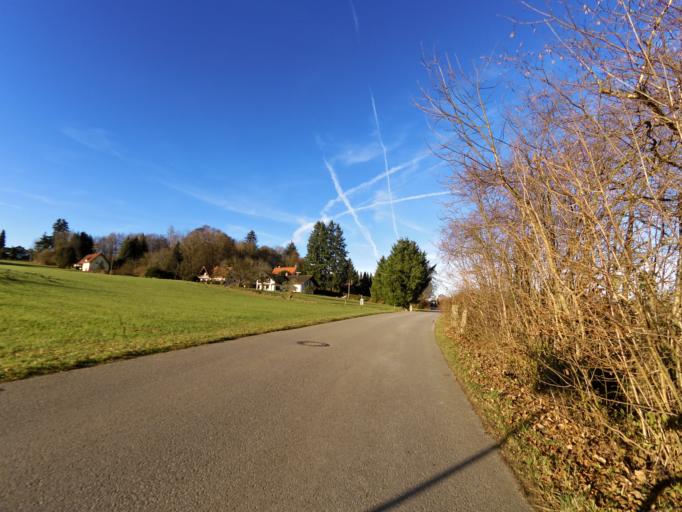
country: DE
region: Bavaria
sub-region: Upper Bavaria
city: Icking
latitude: 47.9604
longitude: 11.4382
